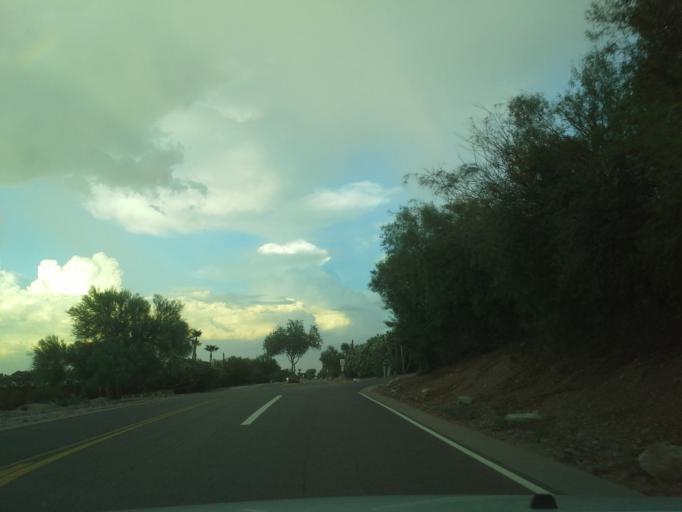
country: US
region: Arizona
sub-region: Maricopa County
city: Paradise Valley
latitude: 33.5238
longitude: -111.9688
